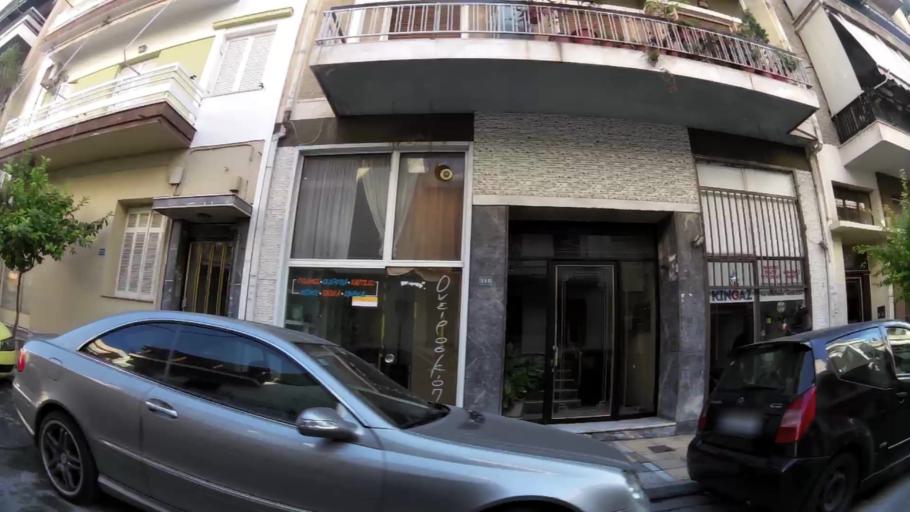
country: GR
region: Attica
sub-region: Nomarchia Athinas
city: Athens
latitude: 37.9668
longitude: 23.7068
